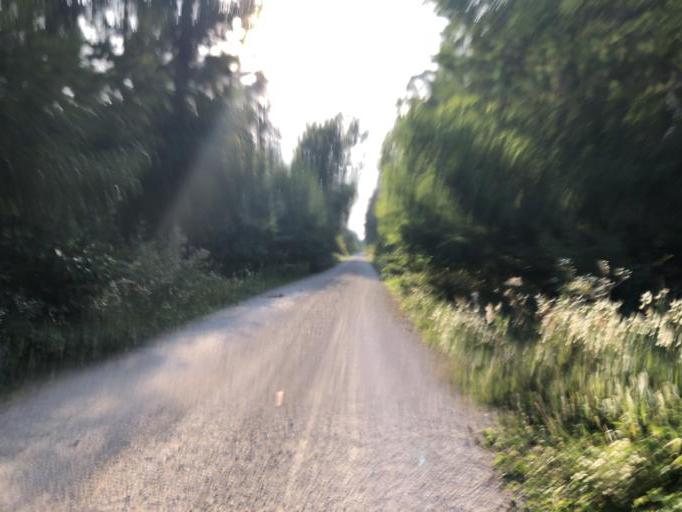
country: DE
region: Bavaria
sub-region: Regierungsbezirk Mittelfranken
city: Uttenreuth
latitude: 49.5788
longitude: 11.0770
